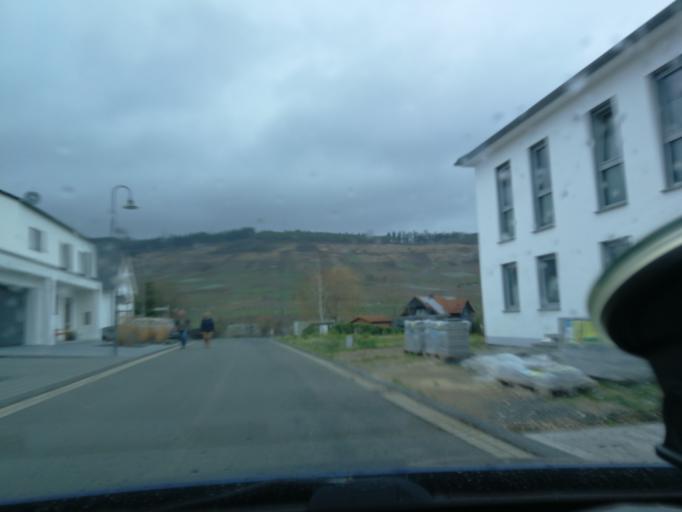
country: DE
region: Rheinland-Pfalz
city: Mehring
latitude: 49.7970
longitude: 6.8170
